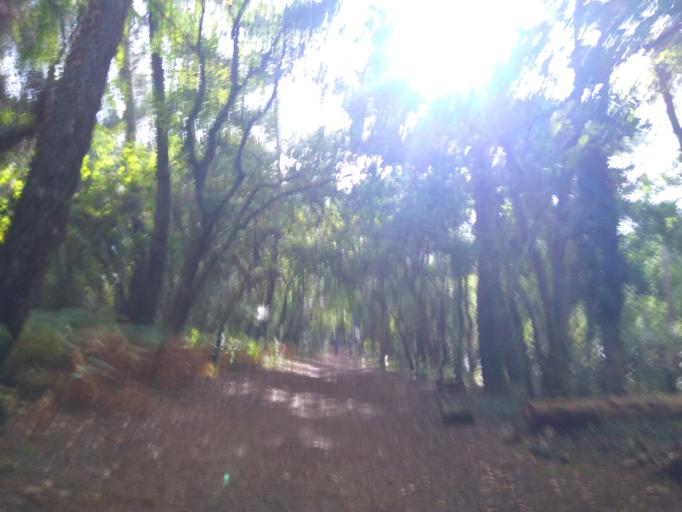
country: FR
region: Aquitaine
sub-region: Departement des Landes
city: Capbreton
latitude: 43.6321
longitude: -1.4424
